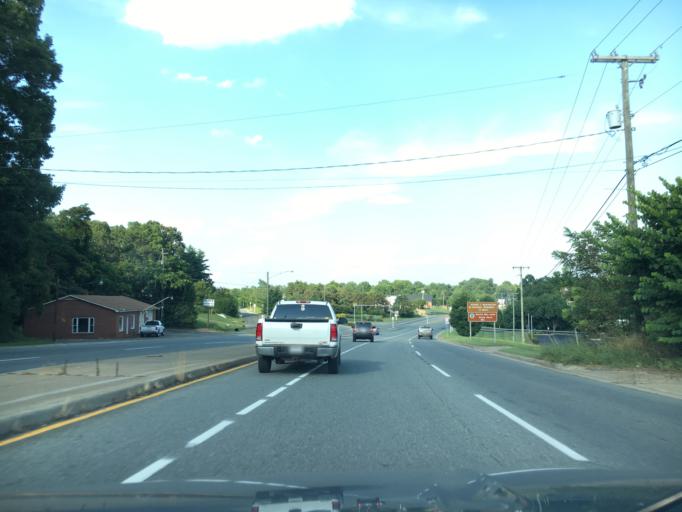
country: US
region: Virginia
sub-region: Franklin County
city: Rocky Mount
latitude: 37.0175
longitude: -79.8605
